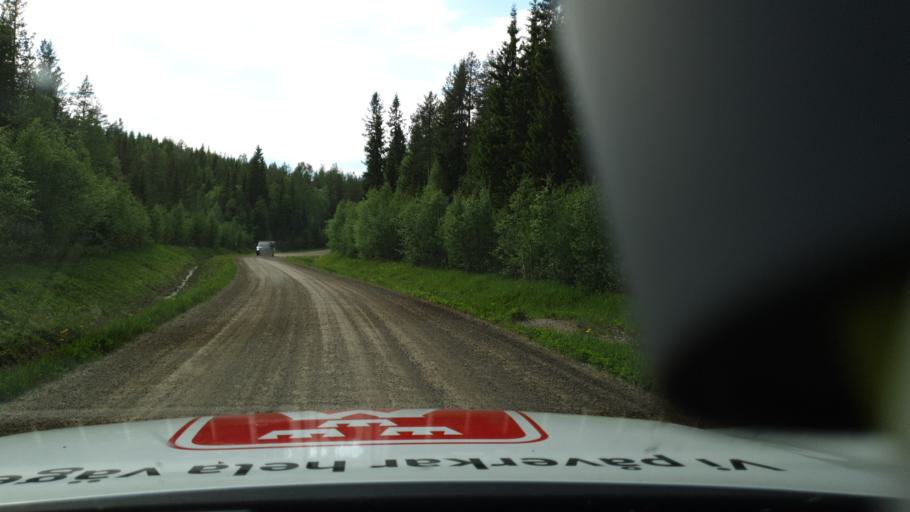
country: SE
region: Jaemtland
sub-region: OEstersunds Kommun
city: Brunflo
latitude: 62.9466
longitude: 14.9494
